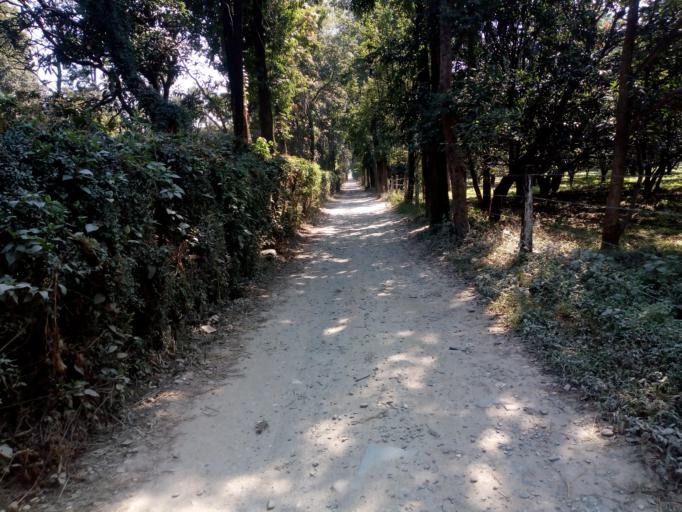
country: IN
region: Uttarakhand
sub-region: Dehradun
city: Harbatpur
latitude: 30.4457
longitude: 77.7448
